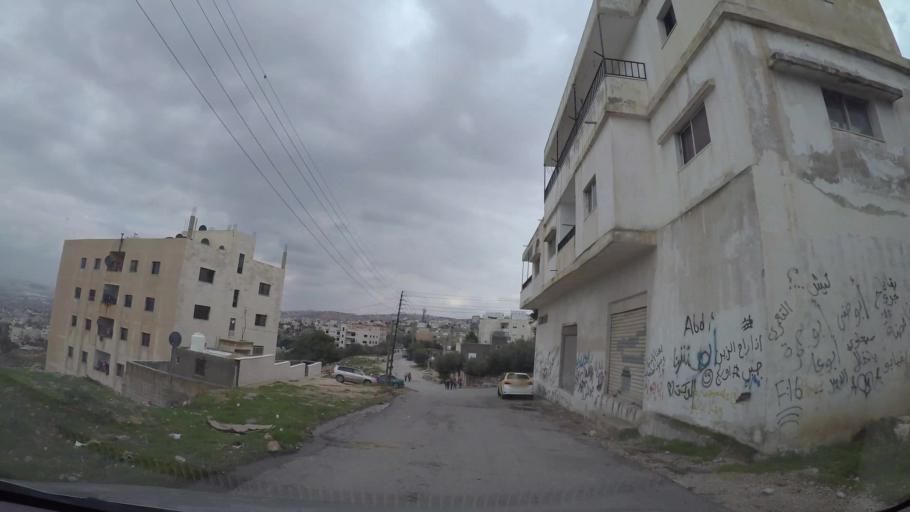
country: JO
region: Amman
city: Al Jubayhah
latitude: 32.0384
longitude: 35.8297
